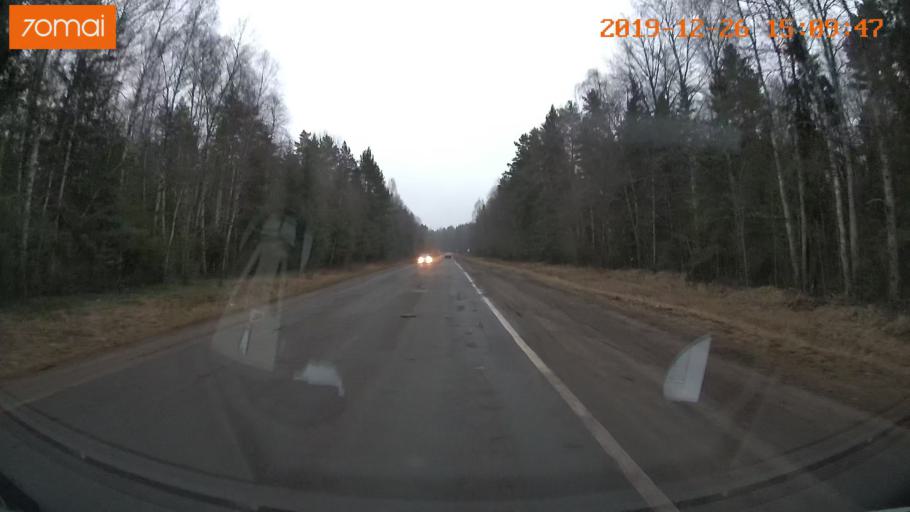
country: RU
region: Jaroslavl
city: Rybinsk
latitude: 58.1460
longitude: 38.8443
